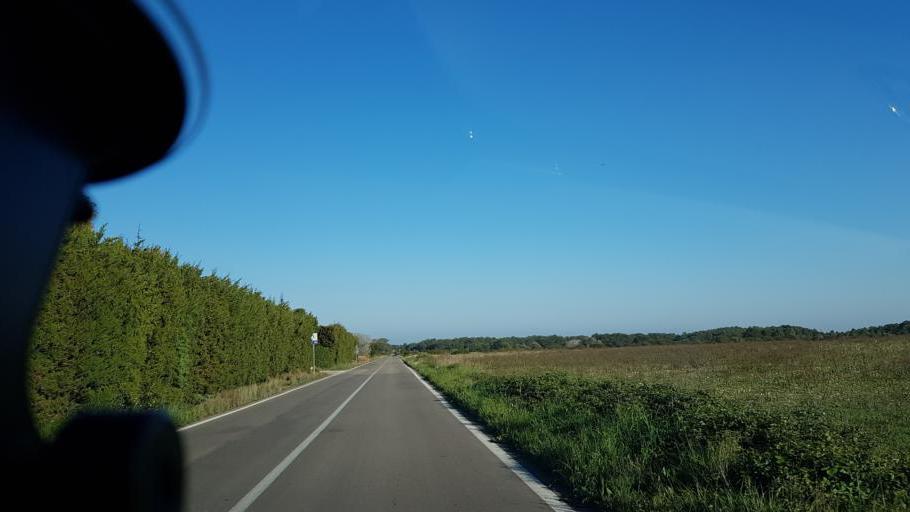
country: IT
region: Apulia
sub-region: Provincia di Lecce
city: Struda
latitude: 40.3922
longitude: 18.2821
